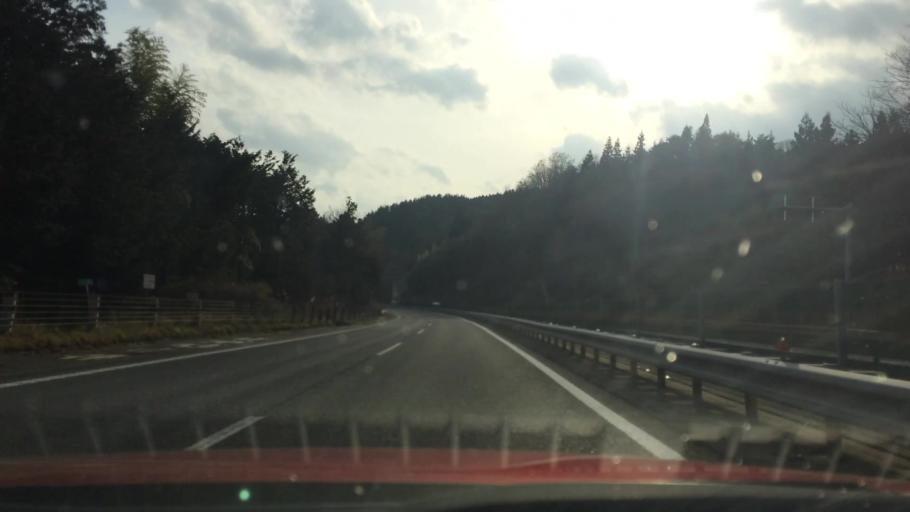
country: JP
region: Nagano
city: Iida
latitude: 35.6455
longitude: 137.8959
